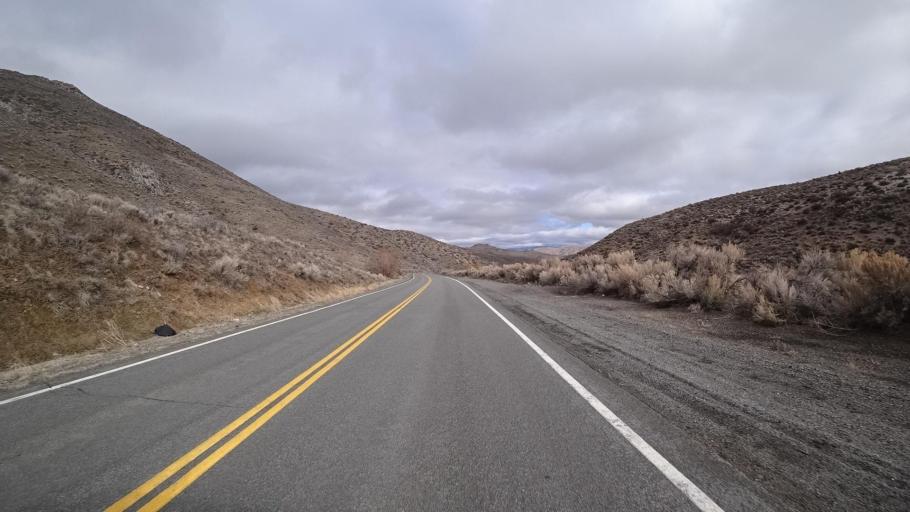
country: US
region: Nevada
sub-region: Washoe County
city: Cold Springs
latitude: 39.8161
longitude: -119.9348
